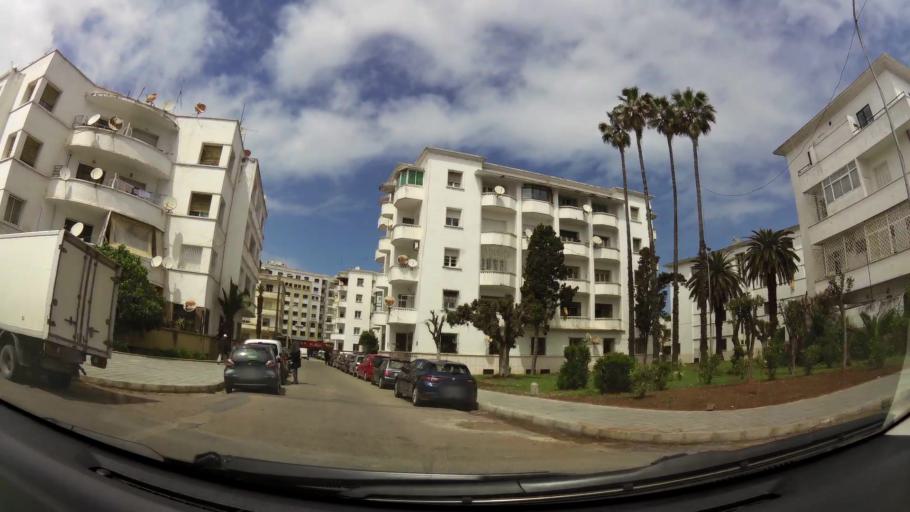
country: MA
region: Grand Casablanca
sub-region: Casablanca
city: Casablanca
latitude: 33.5943
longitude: -7.6388
